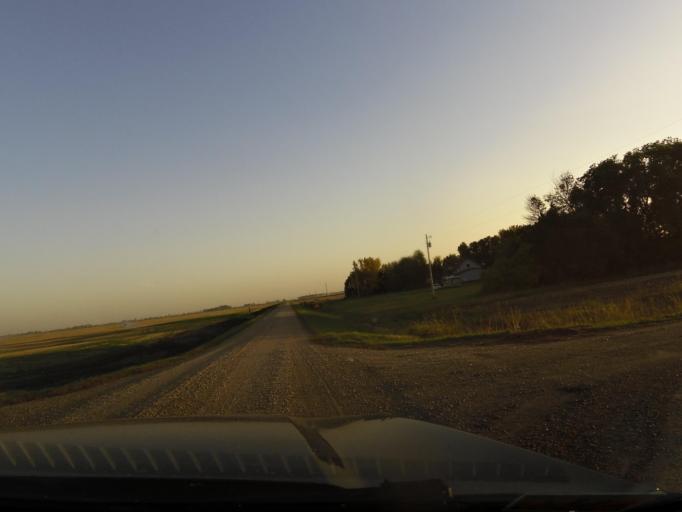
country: US
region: North Dakota
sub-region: Walsh County
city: Grafton
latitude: 48.3831
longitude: -97.2554
